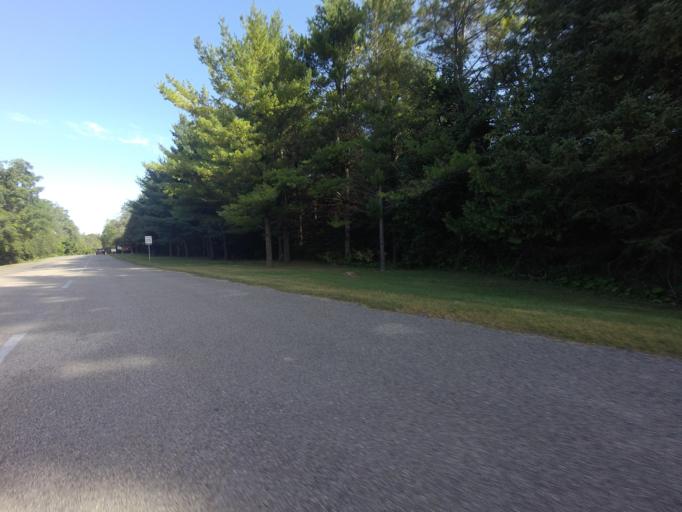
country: CA
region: Ontario
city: Waterloo
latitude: 43.6697
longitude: -80.4418
